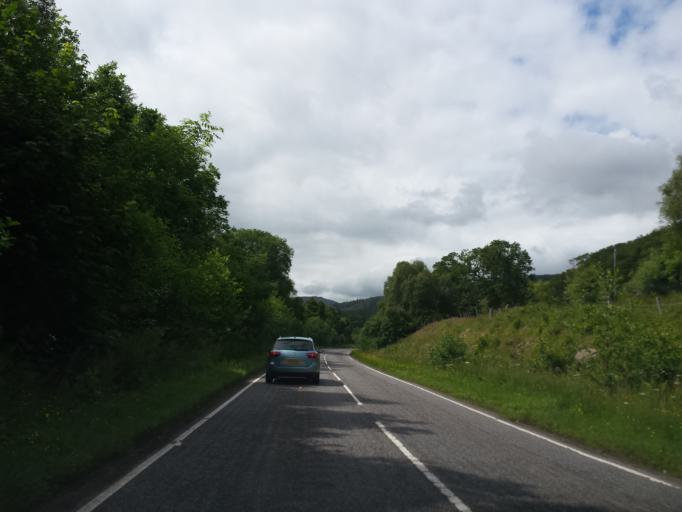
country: GB
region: Scotland
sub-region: Highland
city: Fort William
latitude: 56.8506
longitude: -5.1693
